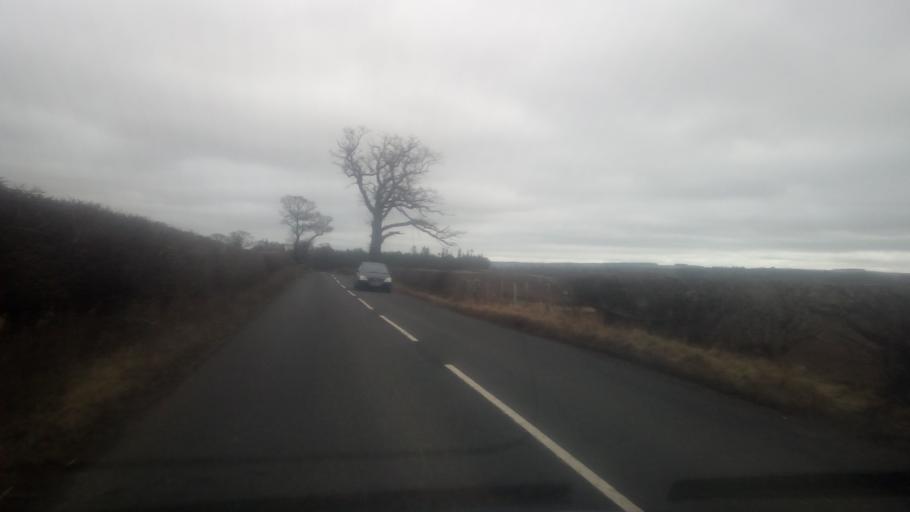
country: GB
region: Scotland
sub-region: The Scottish Borders
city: Kelso
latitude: 55.5884
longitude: -2.4831
